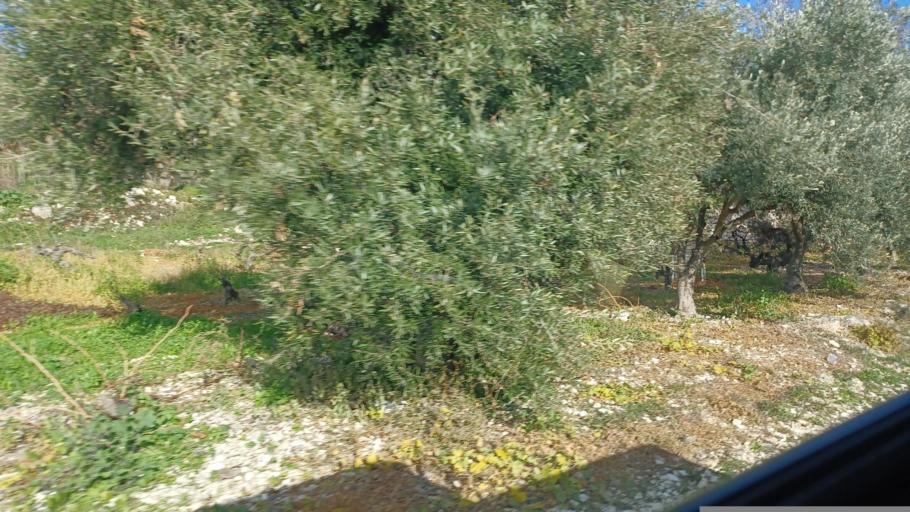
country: CY
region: Limassol
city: Pachna
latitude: 34.8312
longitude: 32.7879
